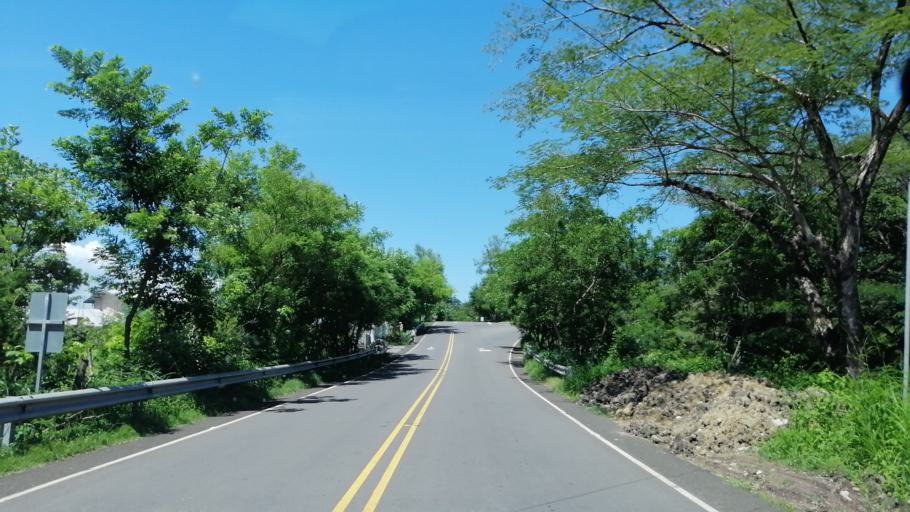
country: SV
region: Morazan
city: Cacaopera
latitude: 13.8087
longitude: -88.1585
